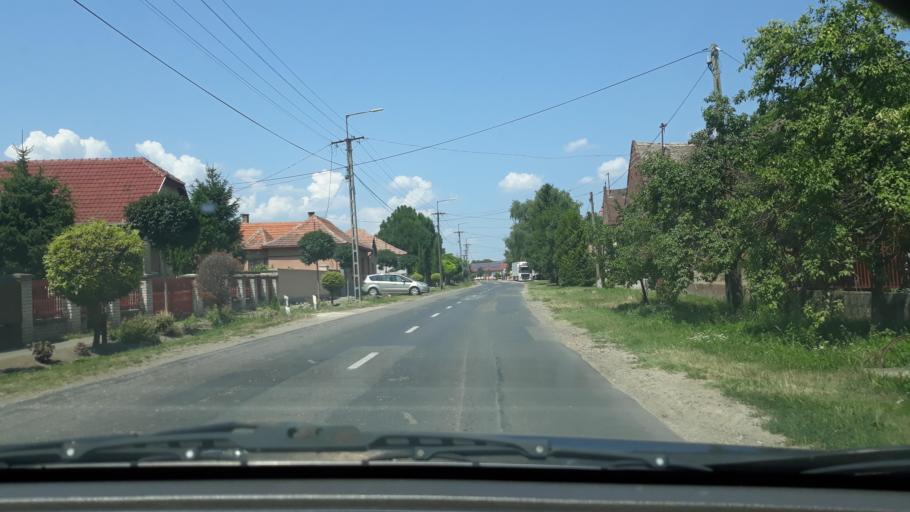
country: HU
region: Hajdu-Bihar
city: Hosszupalyi
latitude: 47.3890
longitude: 21.7337
